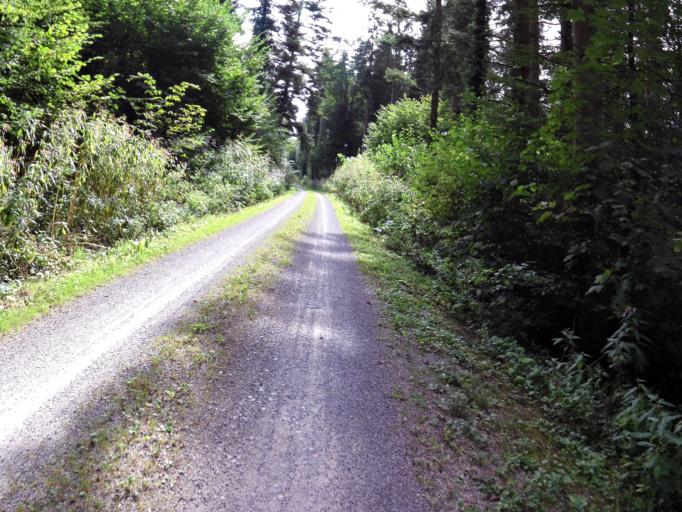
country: DE
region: Baden-Wuerttemberg
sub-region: Freiburg Region
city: Sulz am Neckar
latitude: 48.3428
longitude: 8.5943
